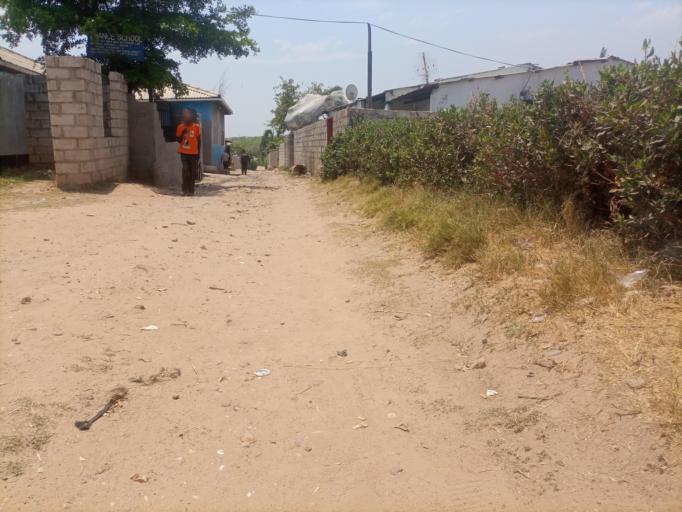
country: ZM
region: Lusaka
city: Lusaka
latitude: -15.4081
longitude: 28.3752
